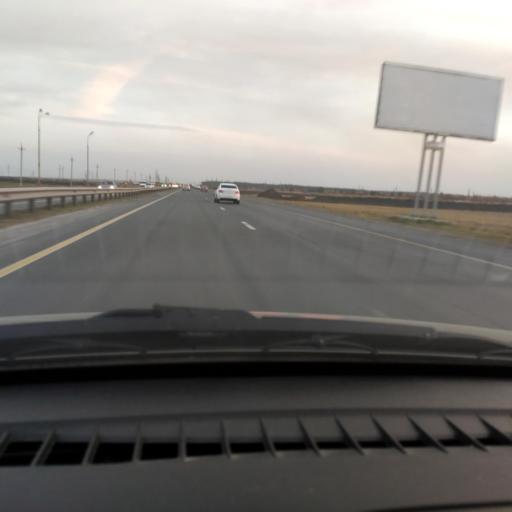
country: RU
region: Samara
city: Zhigulevsk
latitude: 53.5544
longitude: 49.5041
